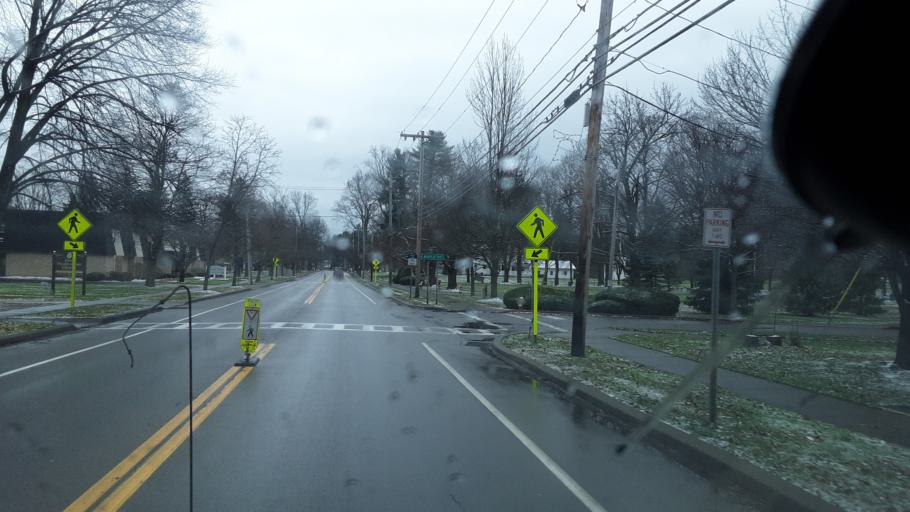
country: US
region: New York
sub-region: Cattaraugus County
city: Portville
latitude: 42.0394
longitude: -78.3413
